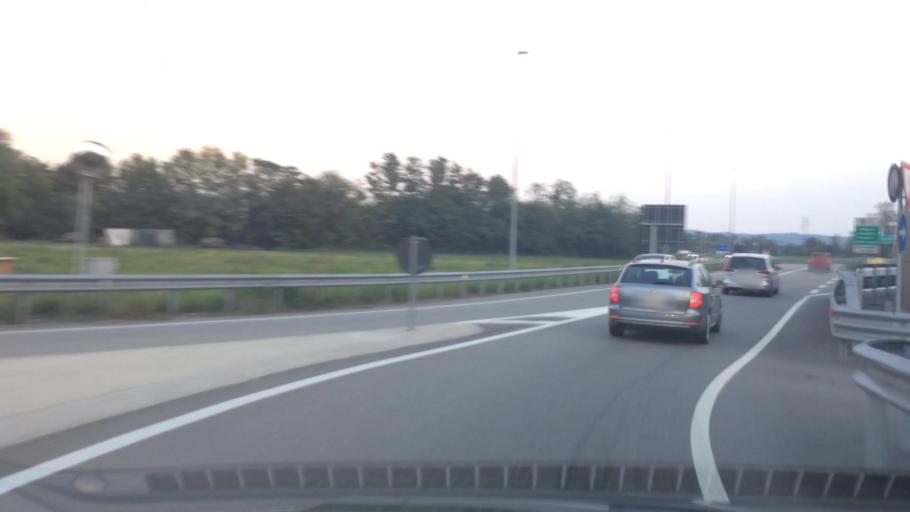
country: IT
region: Lombardy
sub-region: Provincia di Como
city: Casnate Con Bernate
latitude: 45.7750
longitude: 9.0744
